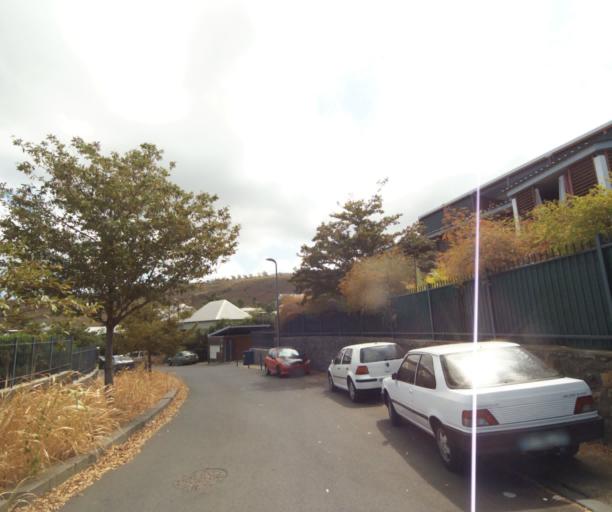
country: RE
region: Reunion
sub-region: Reunion
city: Trois-Bassins
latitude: -21.0859
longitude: 55.2385
